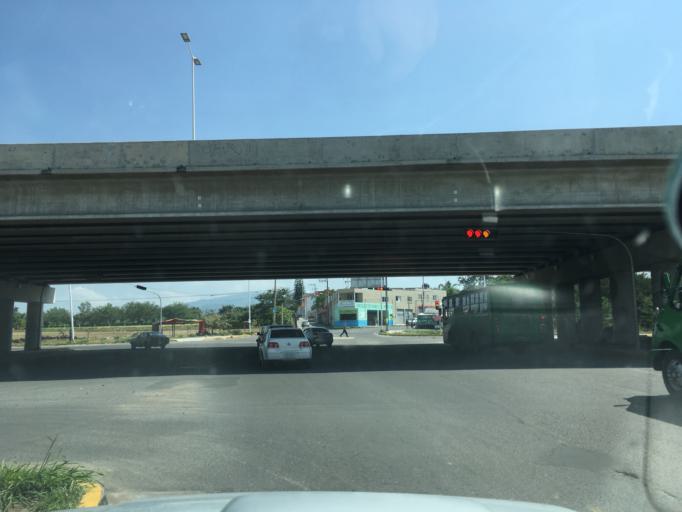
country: MX
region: Jalisco
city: Tonala
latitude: 20.6838
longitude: -103.2453
